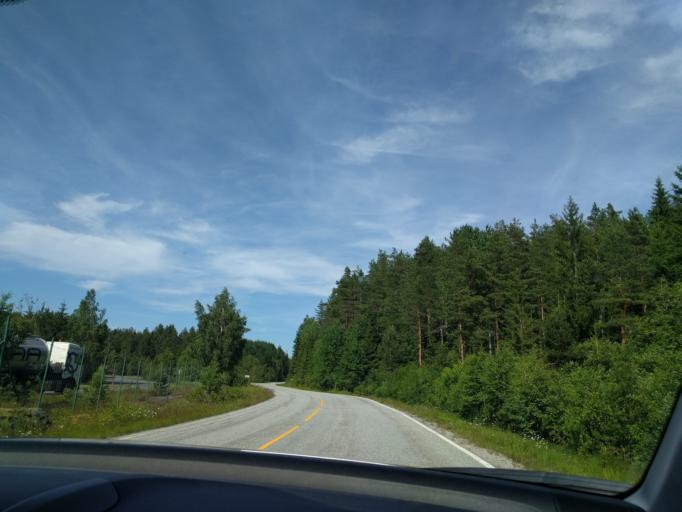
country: NO
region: Aust-Agder
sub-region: Gjerstad
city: Gjerstad
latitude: 58.8597
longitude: 9.1412
